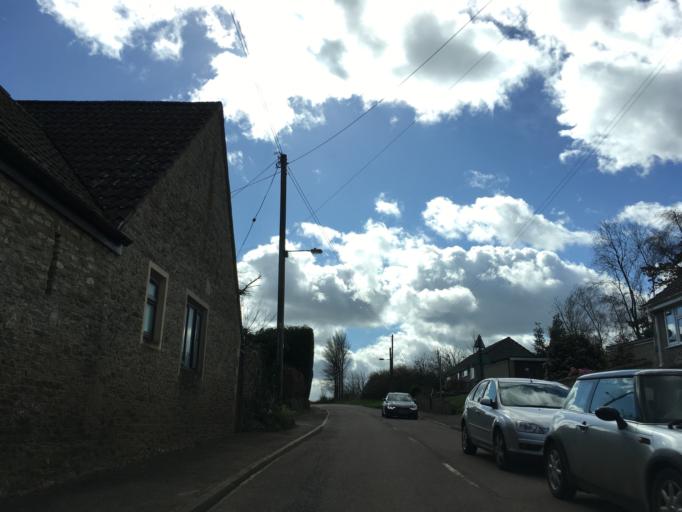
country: GB
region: England
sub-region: South Gloucestershire
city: Marshfield
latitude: 51.5056
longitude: -2.3322
